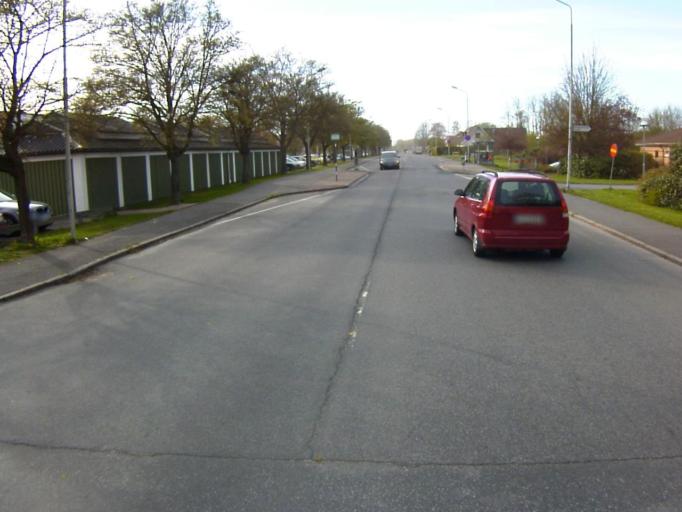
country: SE
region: Skane
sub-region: Kristianstads Kommun
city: Kristianstad
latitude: 56.0597
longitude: 14.1631
